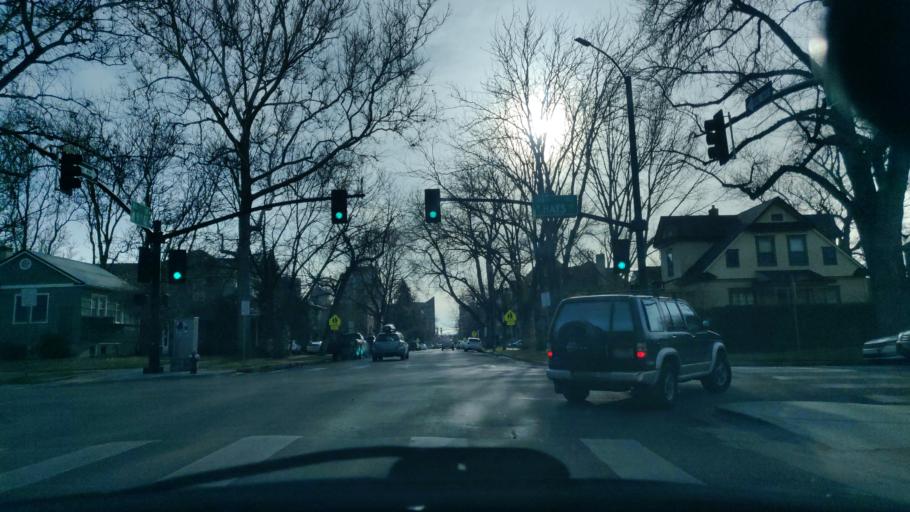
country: US
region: Idaho
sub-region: Ada County
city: Boise
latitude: 43.6218
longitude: -116.1994
